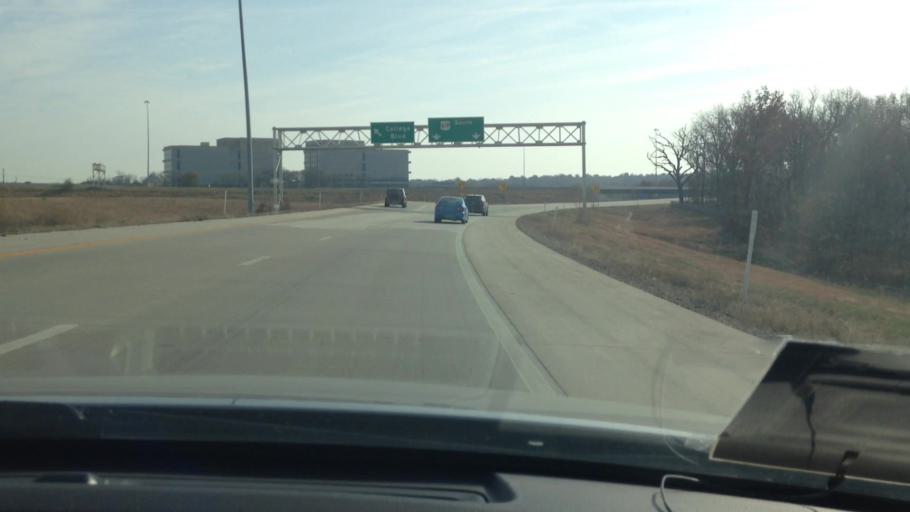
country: US
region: Kansas
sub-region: Johnson County
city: Lenexa
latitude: 38.9345
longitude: -94.7100
